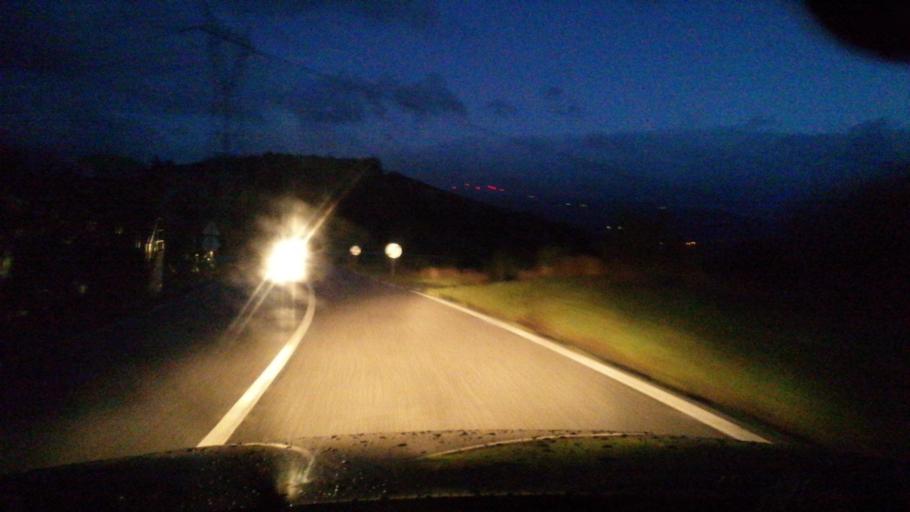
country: PT
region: Viseu
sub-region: Tabuaco
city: Tabuaco
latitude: 41.1246
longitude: -7.5158
